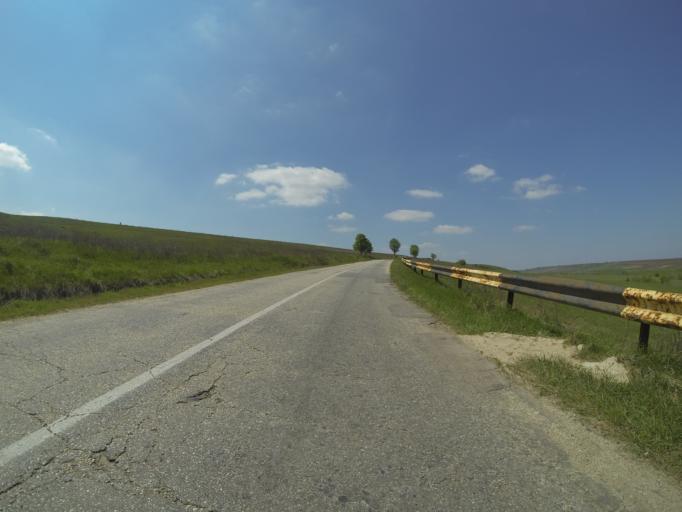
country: RO
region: Dolj
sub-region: Comuna Salcuta
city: Salcuta
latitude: 44.2567
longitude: 23.4471
